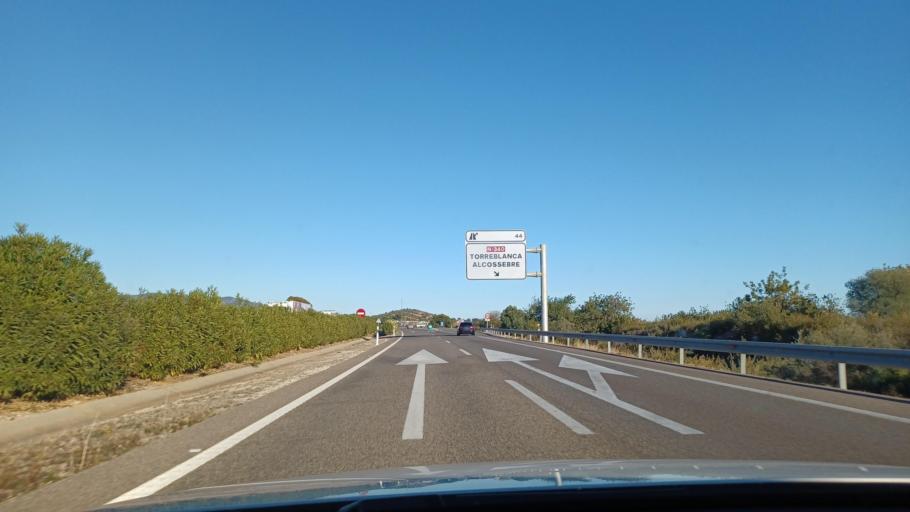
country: ES
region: Valencia
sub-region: Provincia de Castello
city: Torreblanca
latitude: 40.2266
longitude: 0.2001
